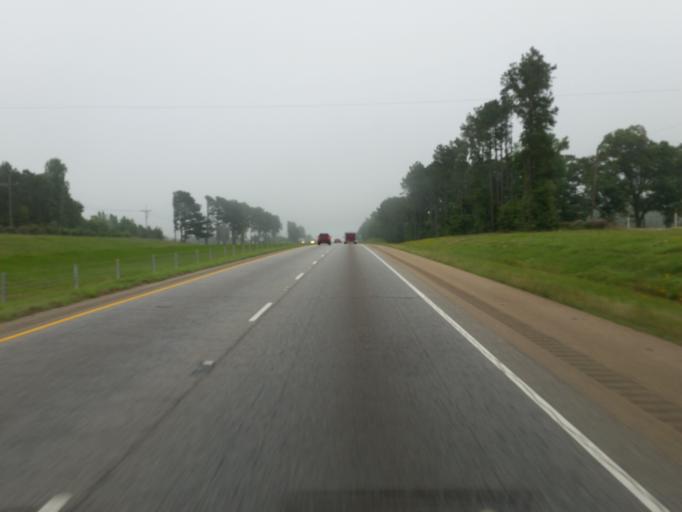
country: US
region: Louisiana
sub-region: Webster Parish
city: Minden
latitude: 32.5859
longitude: -93.2745
